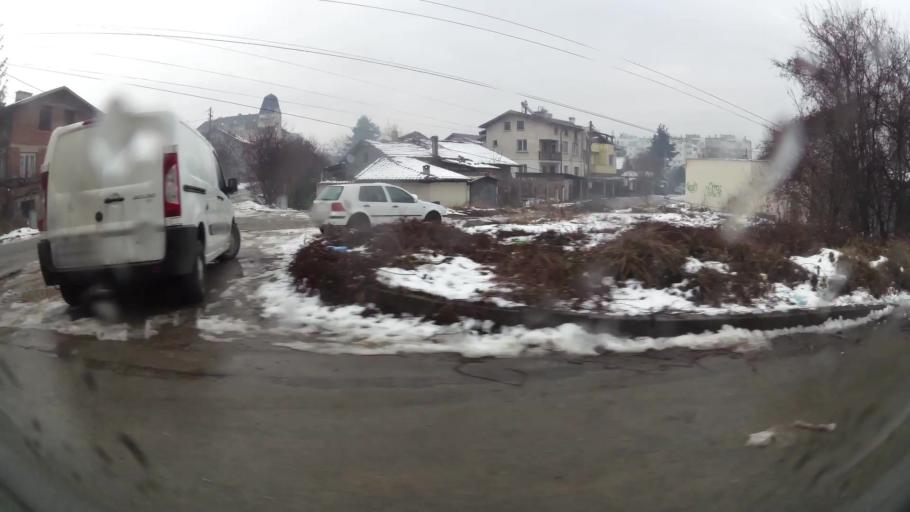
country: BG
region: Sofia-Capital
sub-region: Stolichna Obshtina
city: Sofia
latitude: 42.6756
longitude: 23.2576
